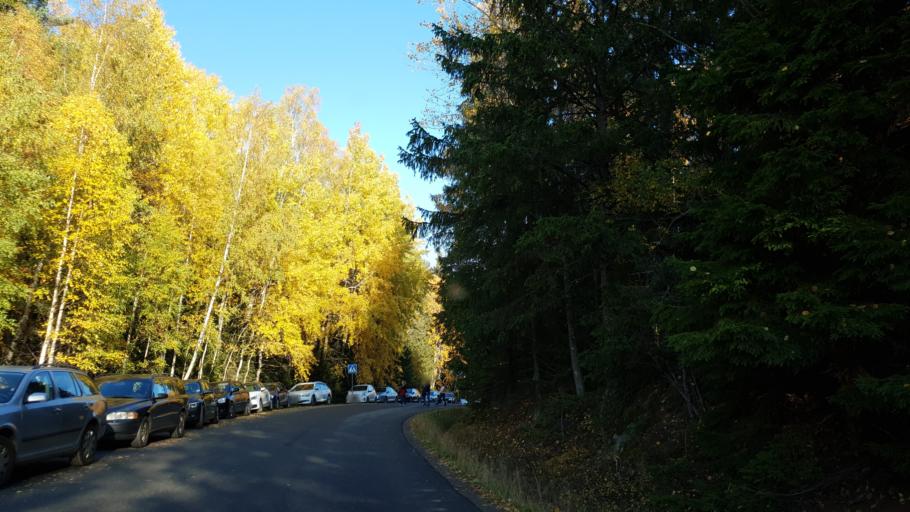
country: SE
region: Stockholm
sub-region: Tyreso Kommun
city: Bollmora
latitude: 59.1693
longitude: 18.2312
